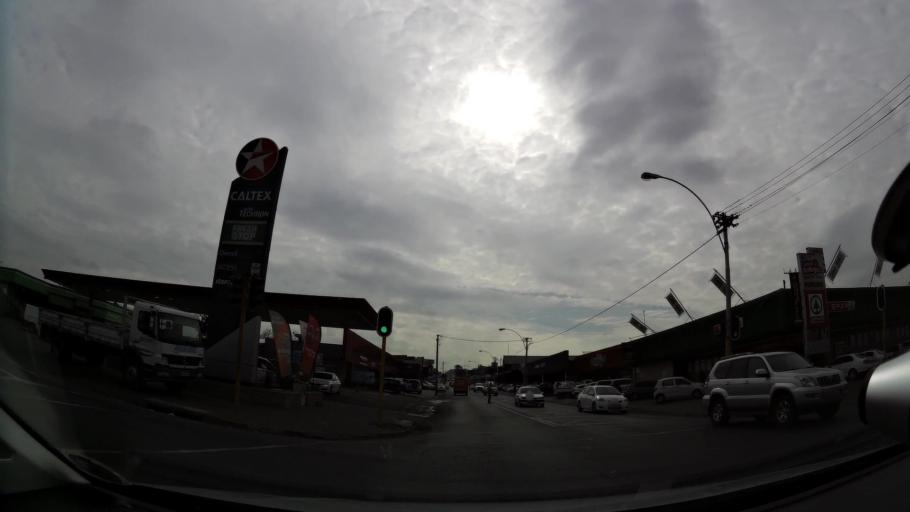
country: ZA
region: Orange Free State
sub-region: Mangaung Metropolitan Municipality
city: Bloemfontein
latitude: -29.1300
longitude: 26.2185
